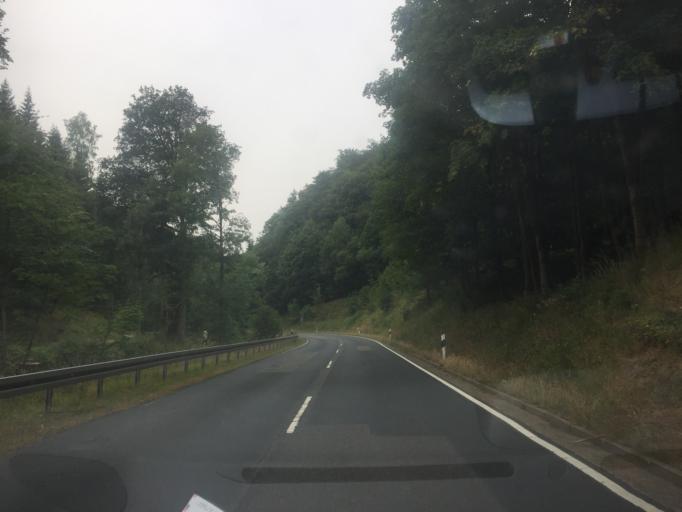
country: DE
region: Lower Saxony
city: Wieda
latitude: 51.6576
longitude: 10.5877
